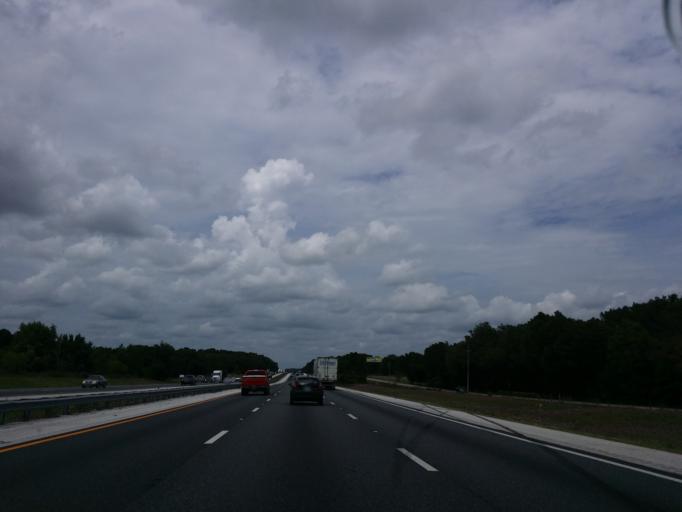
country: US
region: Florida
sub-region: Sumter County
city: Wildwood
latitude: 28.9482
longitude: -82.1173
